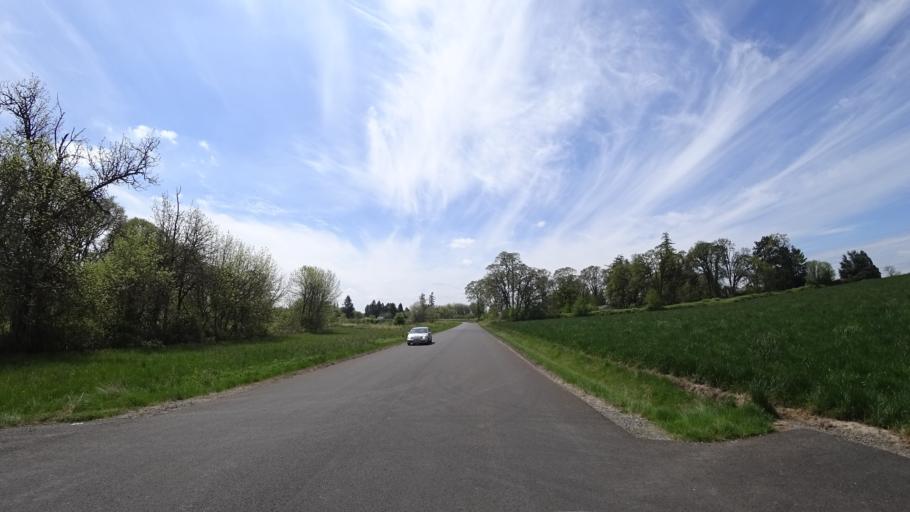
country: US
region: Oregon
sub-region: Washington County
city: Rockcreek
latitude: 45.5679
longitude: -122.9279
